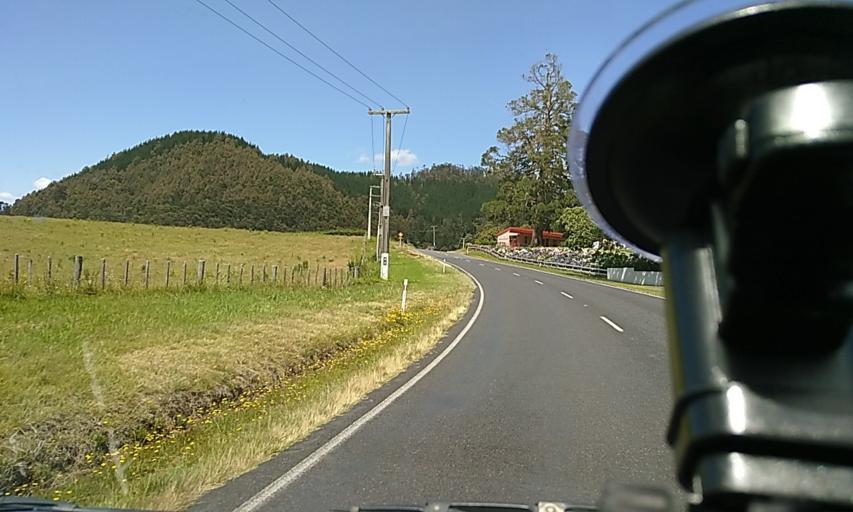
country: NZ
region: Bay of Plenty
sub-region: Western Bay of Plenty District
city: Waihi Beach
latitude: -37.4569
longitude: 175.9328
